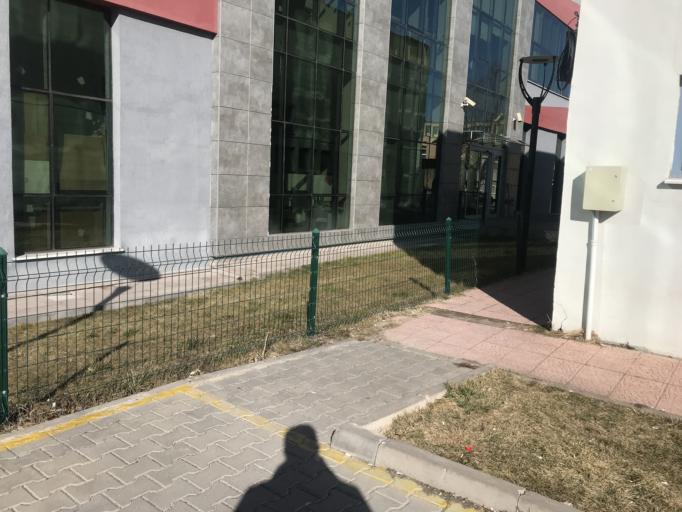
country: TR
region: Eskisehir
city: Eskisehir
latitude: 39.7467
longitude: 30.4744
